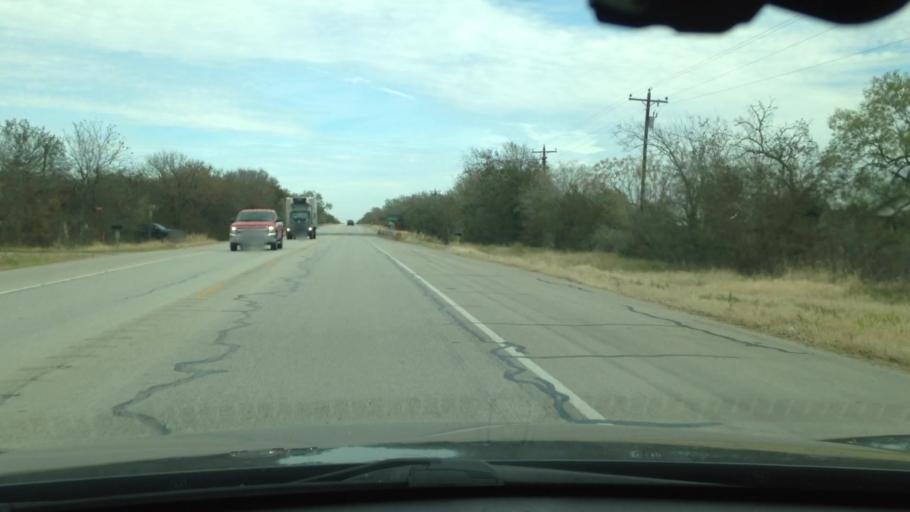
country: US
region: Texas
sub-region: Travis County
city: Garfield
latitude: 30.0598
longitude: -97.6047
